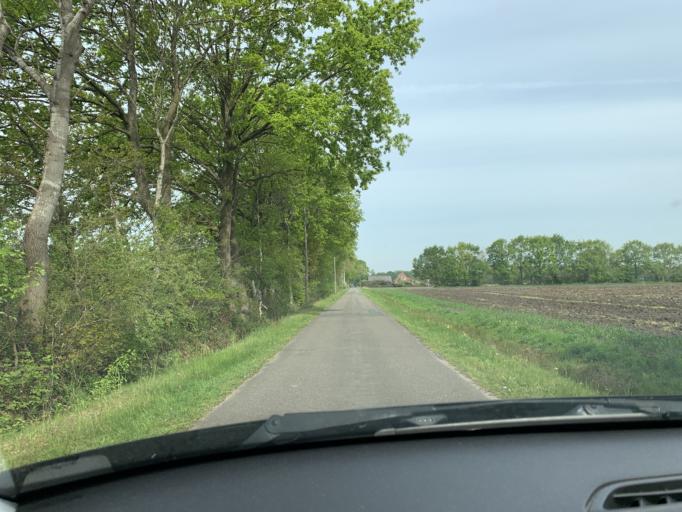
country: DE
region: Lower Saxony
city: Apen
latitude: 53.2314
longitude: 7.8409
